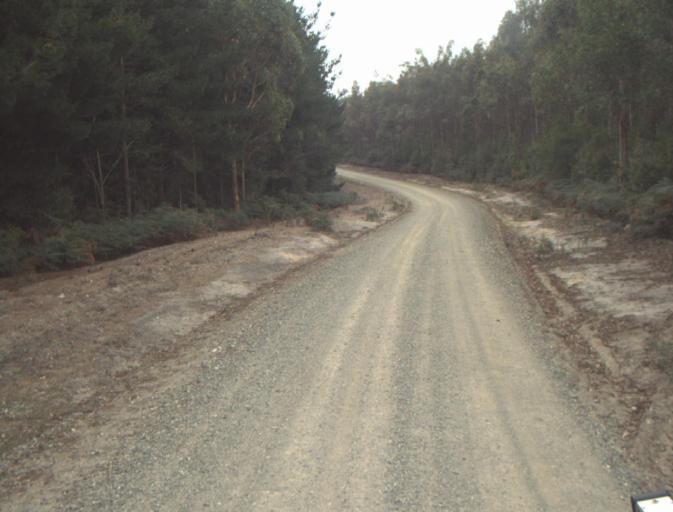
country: AU
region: Tasmania
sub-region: Launceston
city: Mayfield
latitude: -41.1660
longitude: 147.1808
